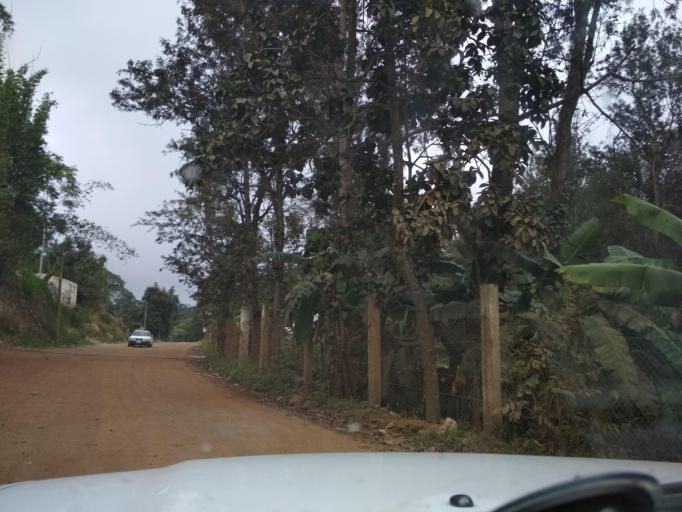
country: MX
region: Veracruz
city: El Castillo
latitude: 19.5427
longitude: -96.8333
